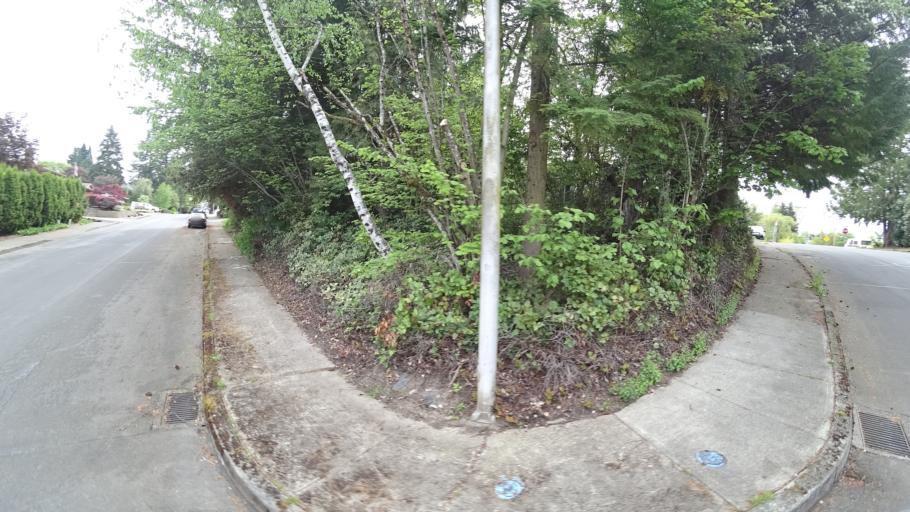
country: US
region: Oregon
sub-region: Washington County
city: Hillsboro
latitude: 45.5287
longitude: -123.0006
